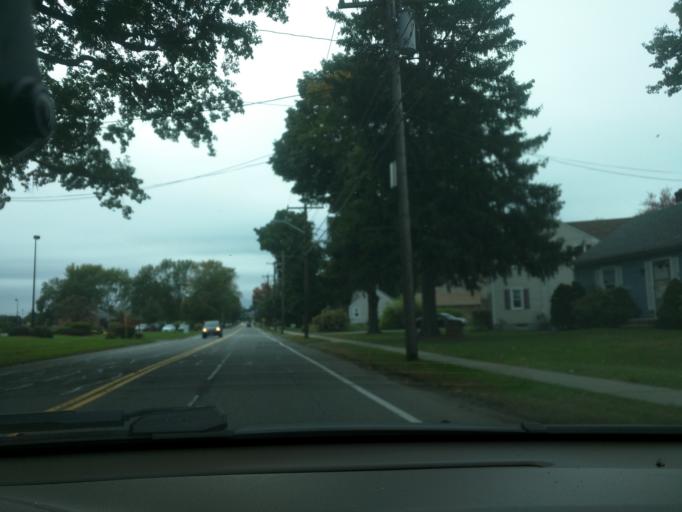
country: US
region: Massachusetts
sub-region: Hampden County
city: East Longmeadow
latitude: 42.0622
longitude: -72.5199
